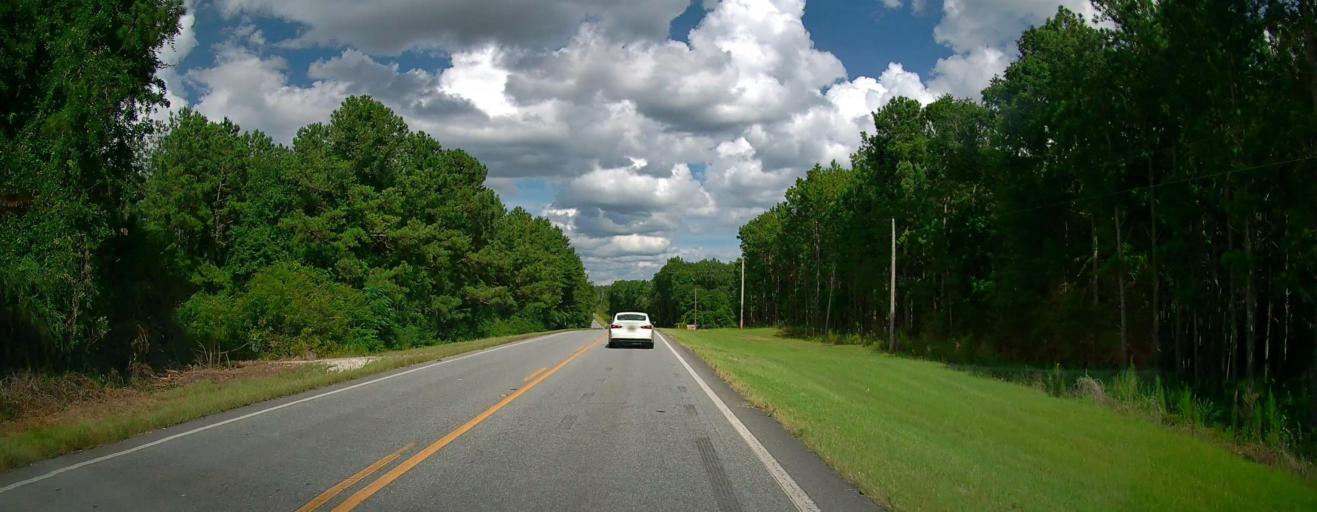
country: US
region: Alabama
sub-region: Lee County
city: Opelika
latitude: 32.4404
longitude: -85.3195
